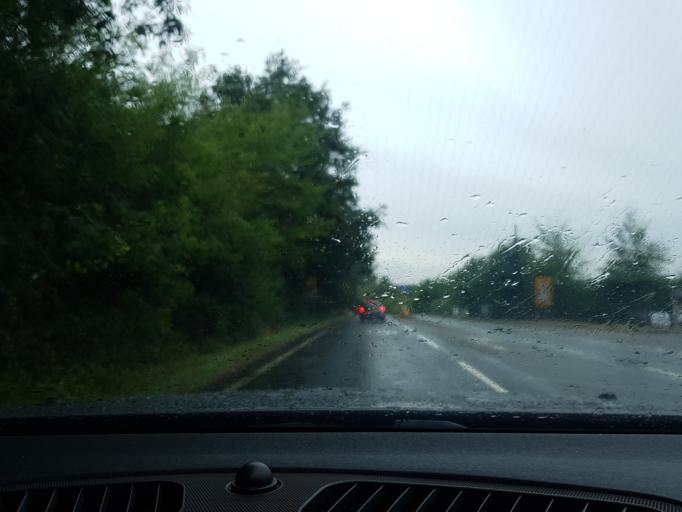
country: GB
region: England
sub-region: Hampshire
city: Fleet
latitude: 51.2426
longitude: -0.8449
